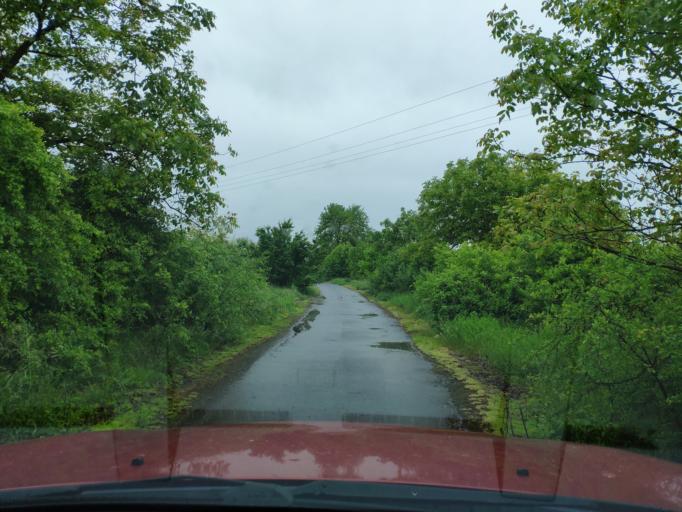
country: SK
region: Kosicky
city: Cierna nad Tisou
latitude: 48.4183
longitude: 22.0568
